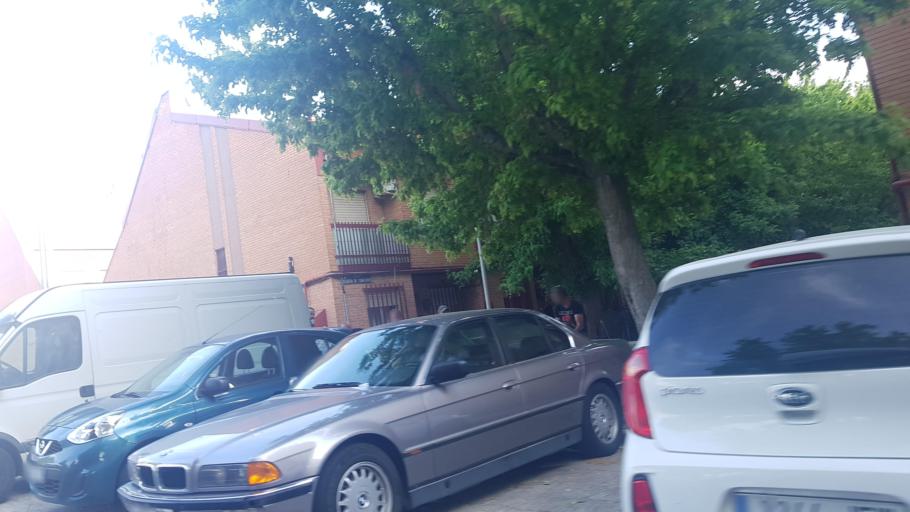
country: ES
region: Madrid
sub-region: Provincia de Madrid
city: Puente de Vallecas
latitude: 40.3726
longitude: -3.6574
